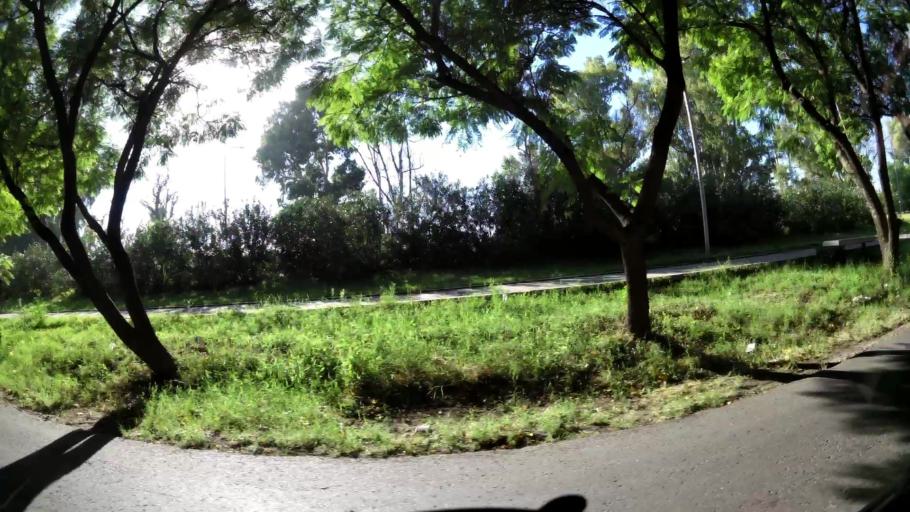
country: AR
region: Mendoza
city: Las Heras
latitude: -32.8580
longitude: -68.8079
